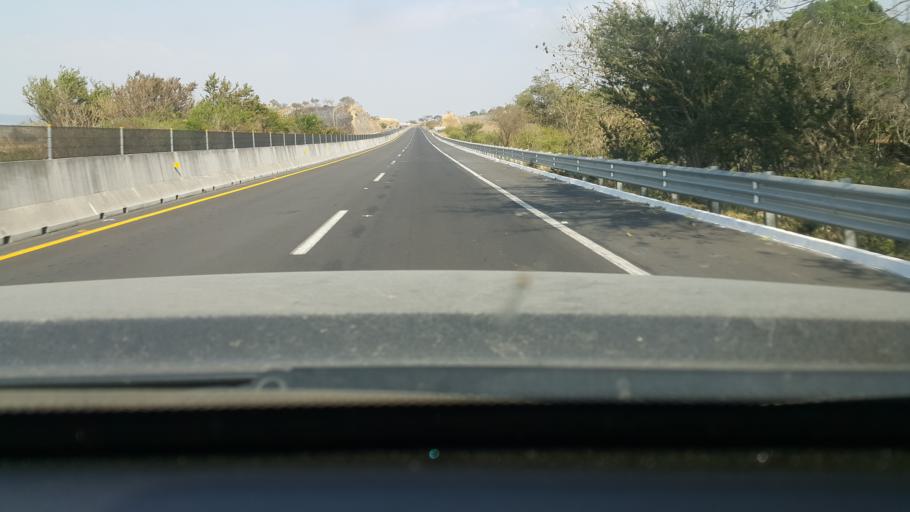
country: MX
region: Nayarit
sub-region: Ahuacatlan
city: Ahuacatlan
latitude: 21.0571
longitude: -104.5298
